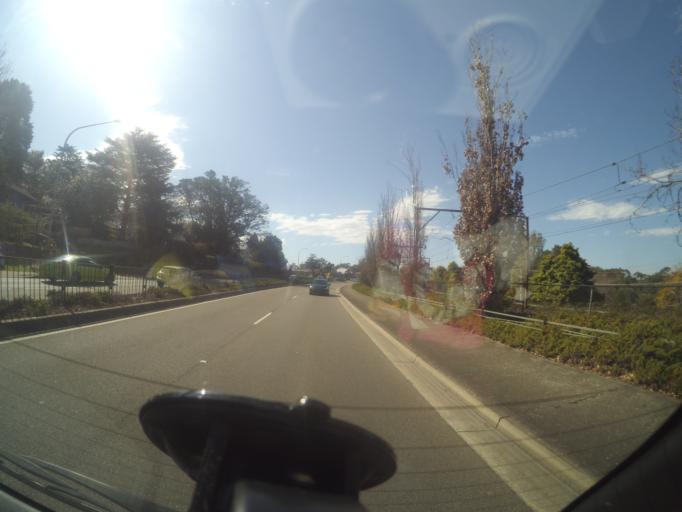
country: AU
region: New South Wales
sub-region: Blue Mountains Municipality
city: Hazelbrook
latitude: -33.6956
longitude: 150.5356
